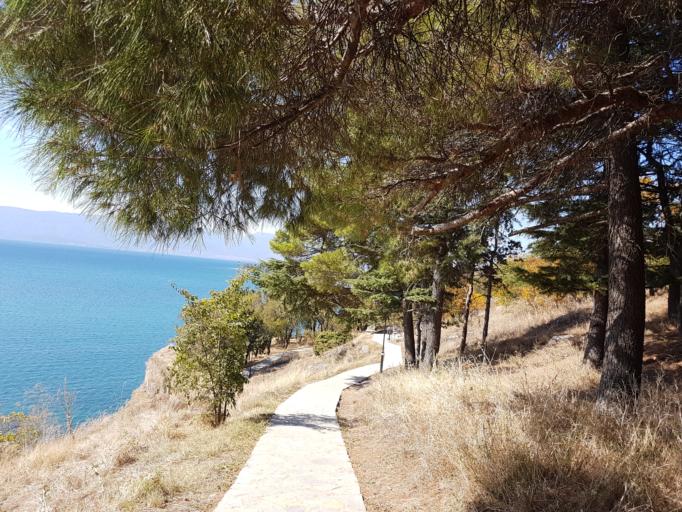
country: MK
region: Ohrid
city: Ohrid
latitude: 41.1141
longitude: 20.7886
